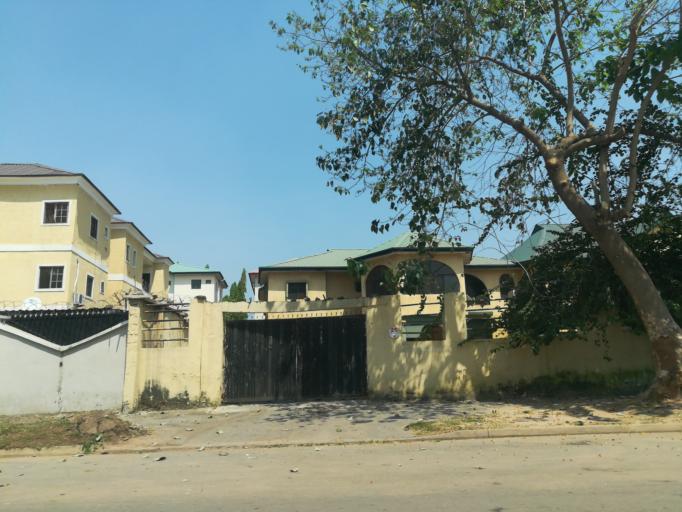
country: NG
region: Abuja Federal Capital Territory
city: Abuja
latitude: 9.0628
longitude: 7.4391
